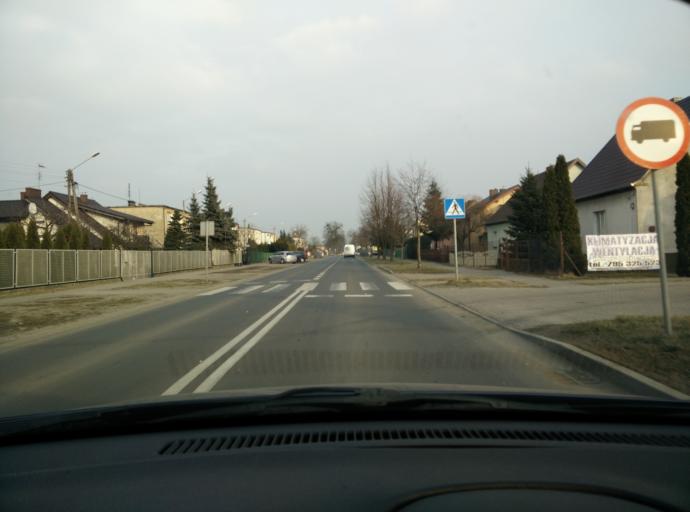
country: PL
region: Greater Poland Voivodeship
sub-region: Powiat sredzki
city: Sroda Wielkopolska
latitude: 52.2321
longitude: 17.2540
